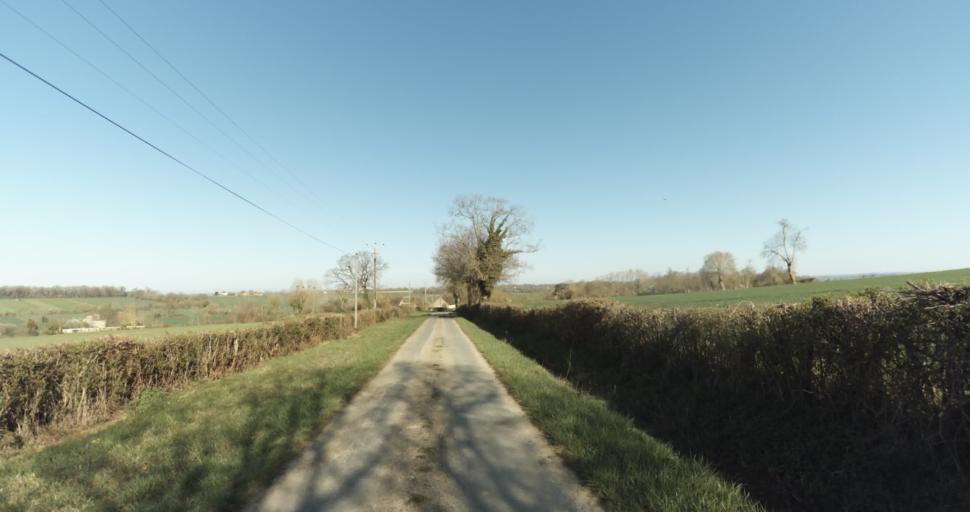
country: FR
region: Lower Normandy
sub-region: Departement du Calvados
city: Saint-Pierre-sur-Dives
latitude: 48.9854
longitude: 0.0153
